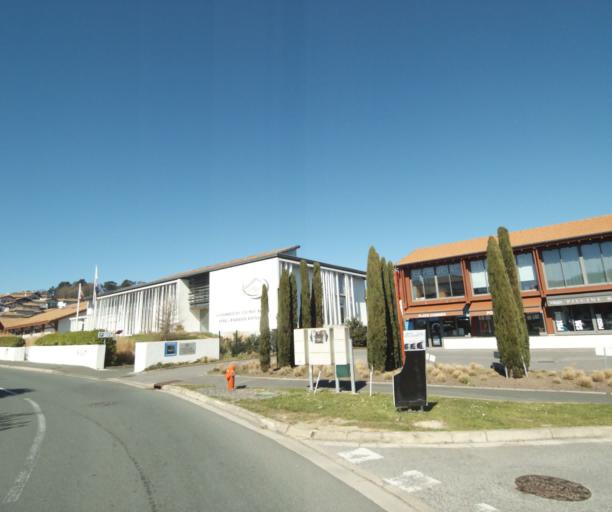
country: FR
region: Aquitaine
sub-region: Departement des Pyrenees-Atlantiques
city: Ciboure
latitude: 43.3837
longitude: -1.6927
